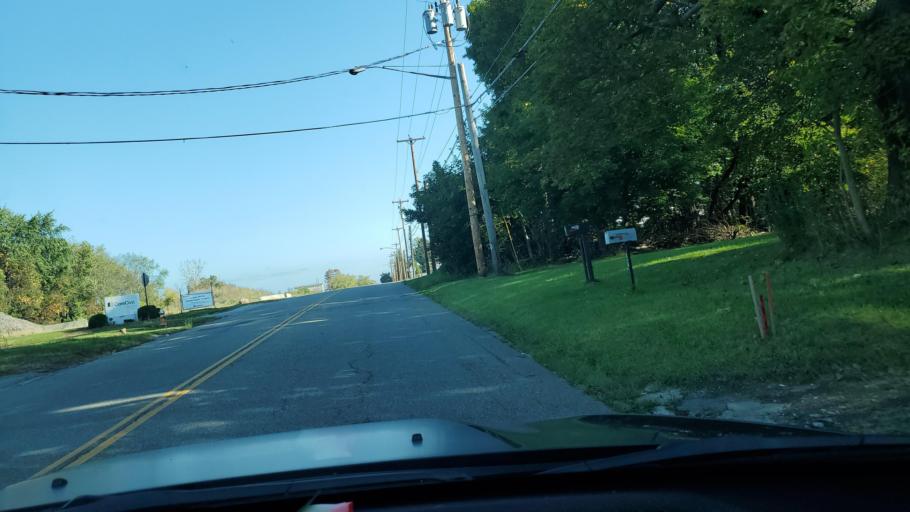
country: US
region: Ohio
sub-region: Mahoning County
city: Youngstown
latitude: 41.1284
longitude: -80.6268
